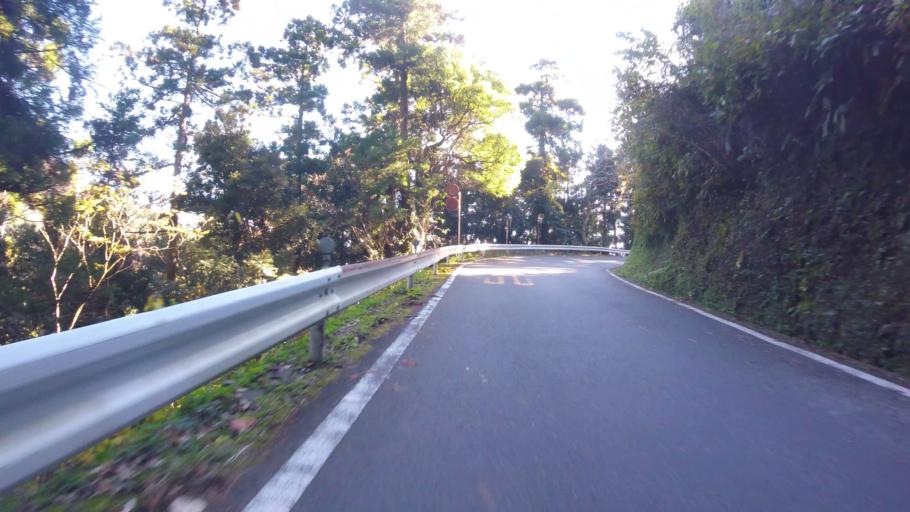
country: JP
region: Shizuoka
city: Shimoda
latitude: 34.7646
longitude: 138.9719
